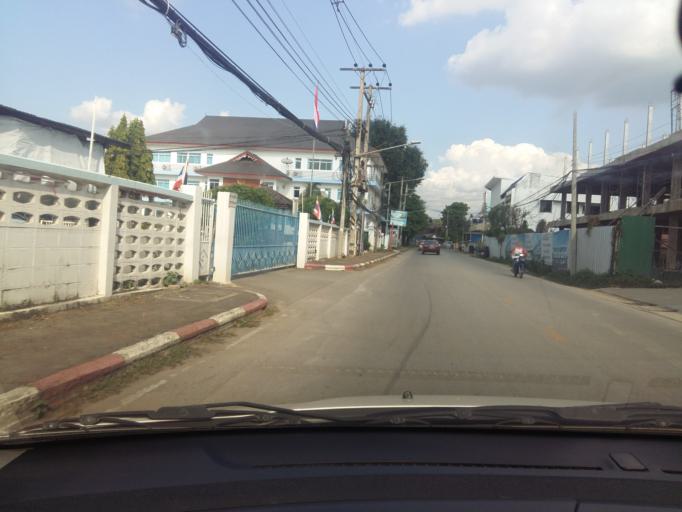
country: TH
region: Lampang
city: Lampang
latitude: 18.2915
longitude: 99.5075
